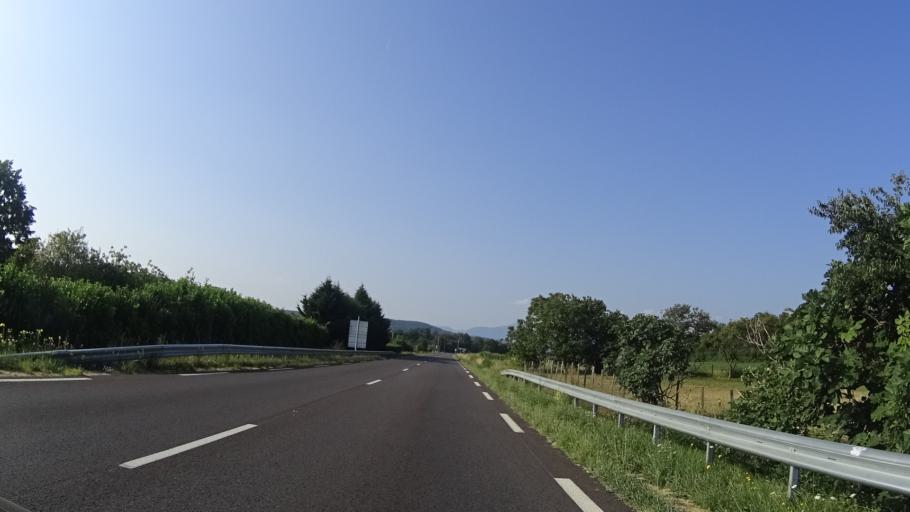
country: FR
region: Midi-Pyrenees
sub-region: Departement de l'Ariege
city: Mirepoix
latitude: 43.0316
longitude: 1.8968
